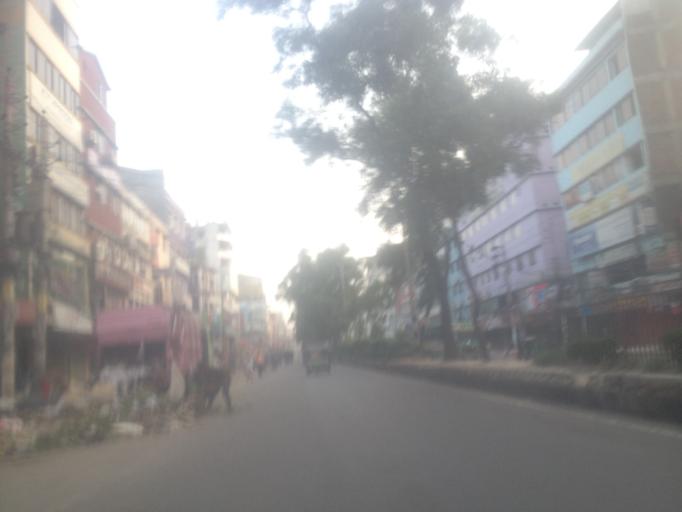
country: BD
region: Dhaka
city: Azimpur
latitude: 23.7920
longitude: 90.3750
